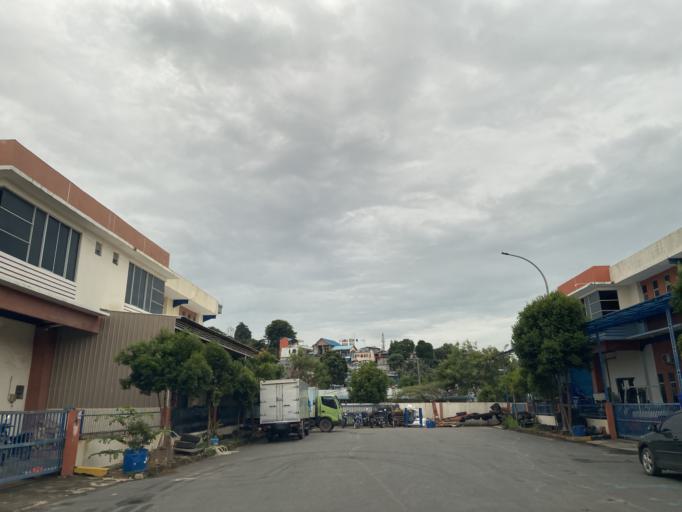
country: SG
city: Singapore
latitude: 1.1674
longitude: 104.0198
